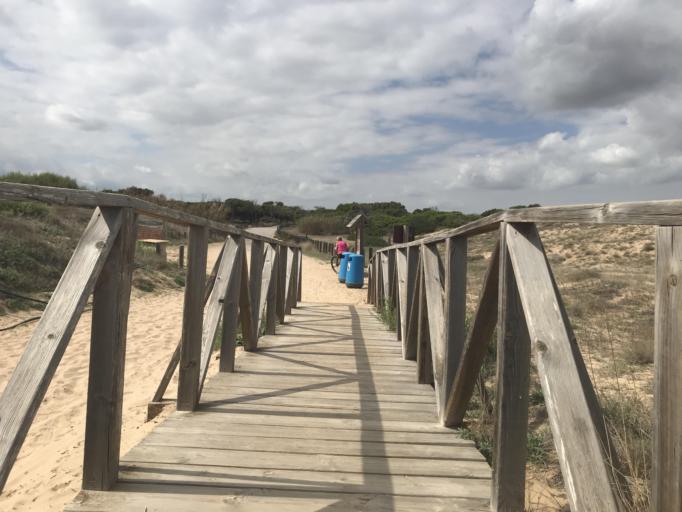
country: ES
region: Valencia
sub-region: Provincia de Alicante
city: Guardamar del Segura
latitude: 38.0471
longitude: -0.6524
